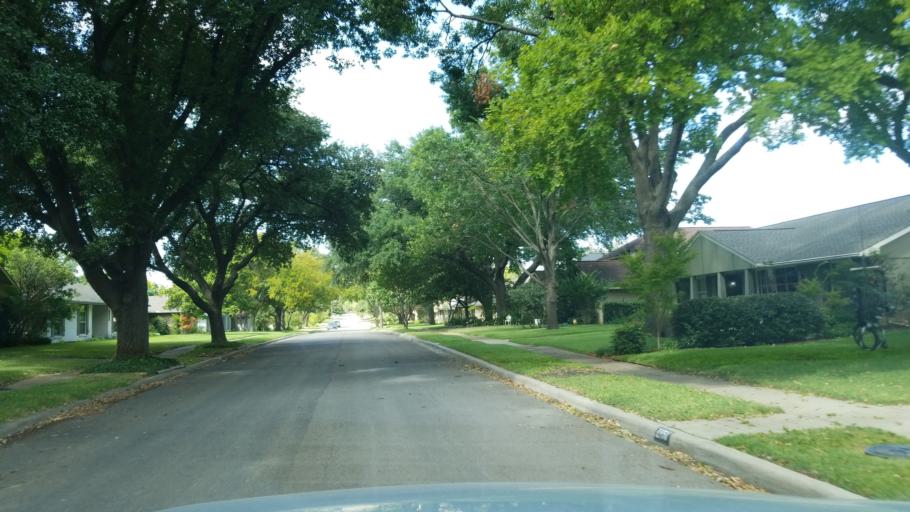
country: US
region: Texas
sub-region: Dallas County
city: Richardson
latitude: 32.9687
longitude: -96.7700
